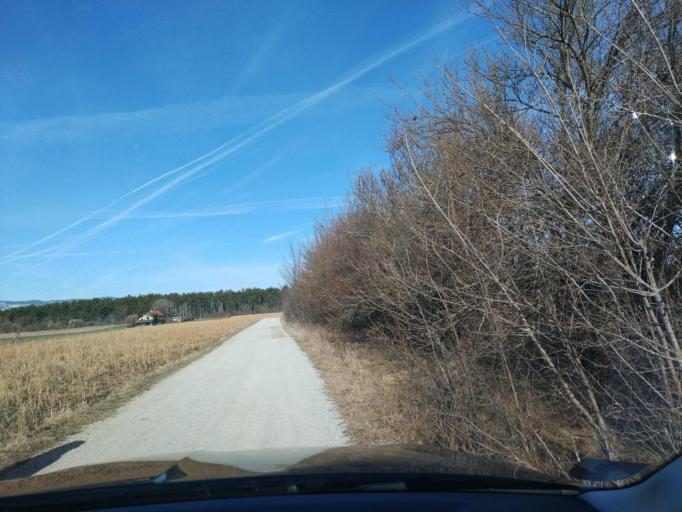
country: AT
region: Lower Austria
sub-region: Politischer Bezirk Neunkirchen
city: Breitenau
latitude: 47.7418
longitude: 16.1669
